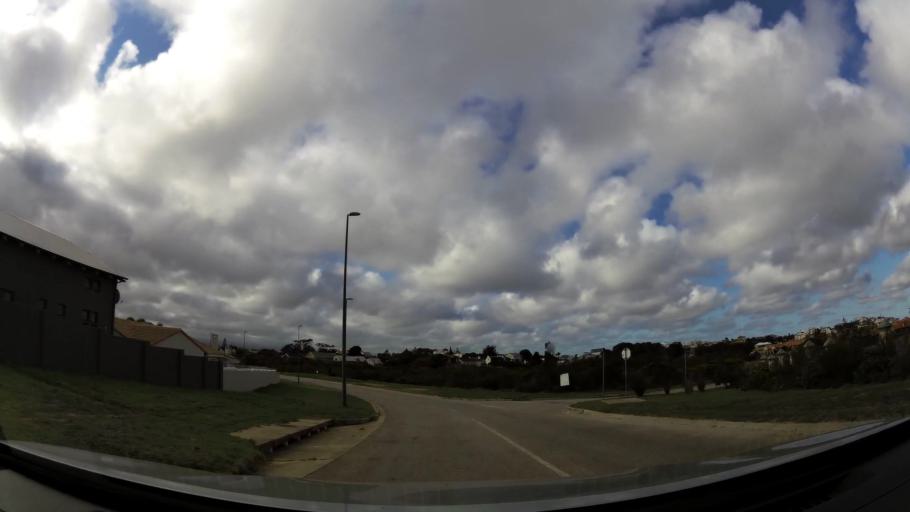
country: ZA
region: Western Cape
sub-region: Eden District Municipality
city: Plettenberg Bay
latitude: -34.0856
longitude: 23.3624
